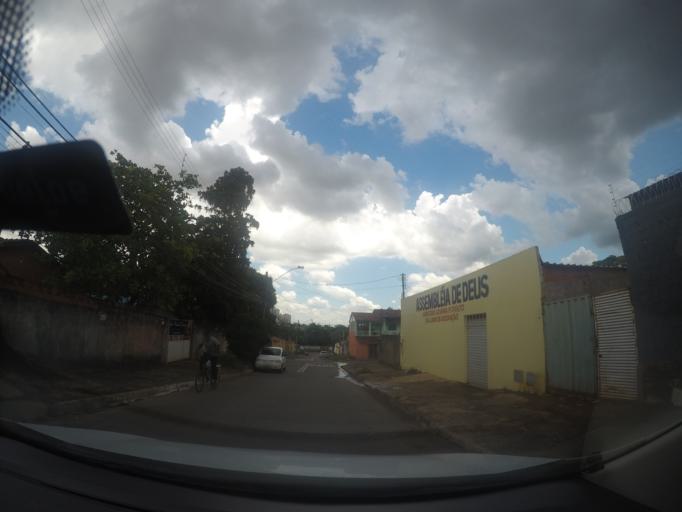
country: BR
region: Goias
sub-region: Goiania
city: Goiania
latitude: -16.7033
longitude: -49.3160
